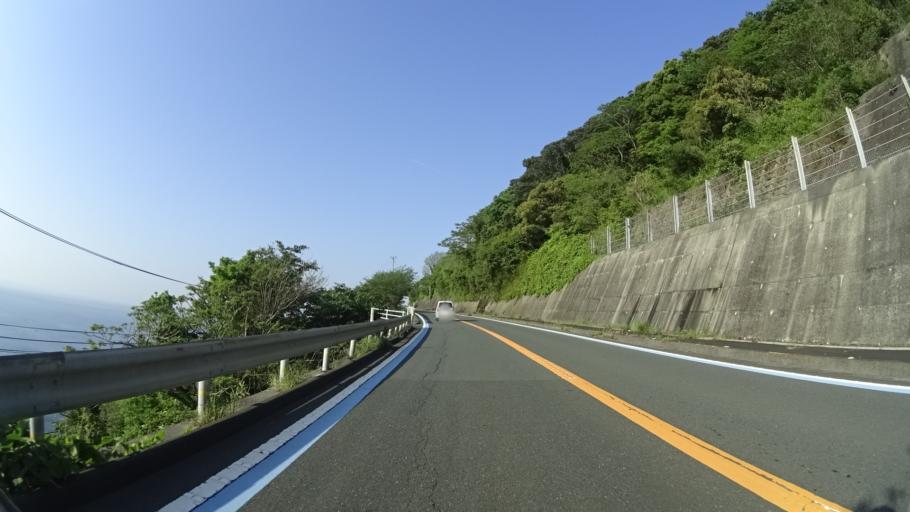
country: JP
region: Ehime
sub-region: Nishiuwa-gun
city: Ikata-cho
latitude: 33.4009
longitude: 132.1658
